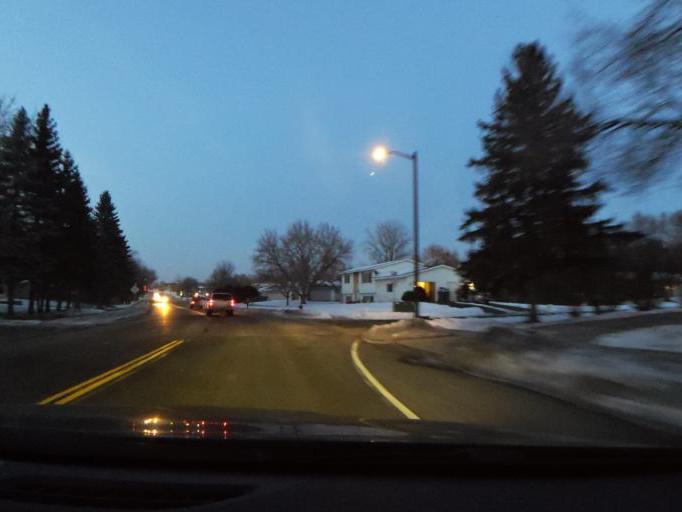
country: US
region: Minnesota
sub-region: Scott County
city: Prior Lake
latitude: 44.7123
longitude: -93.4145
